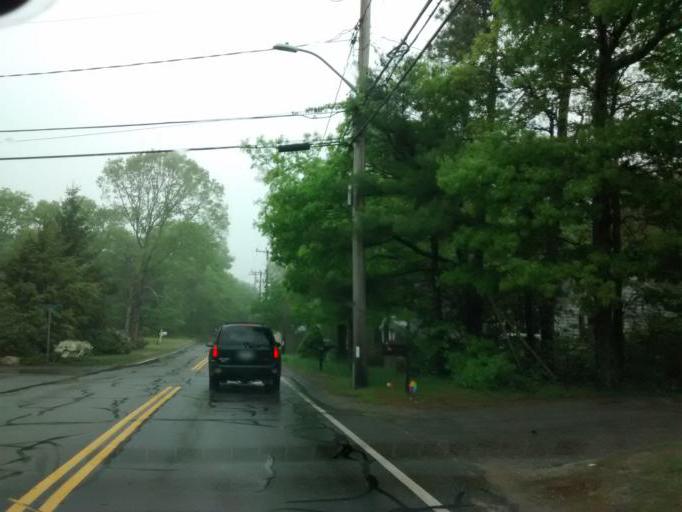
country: US
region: Massachusetts
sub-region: Barnstable County
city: Pocasset
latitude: 41.6895
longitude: -70.6011
